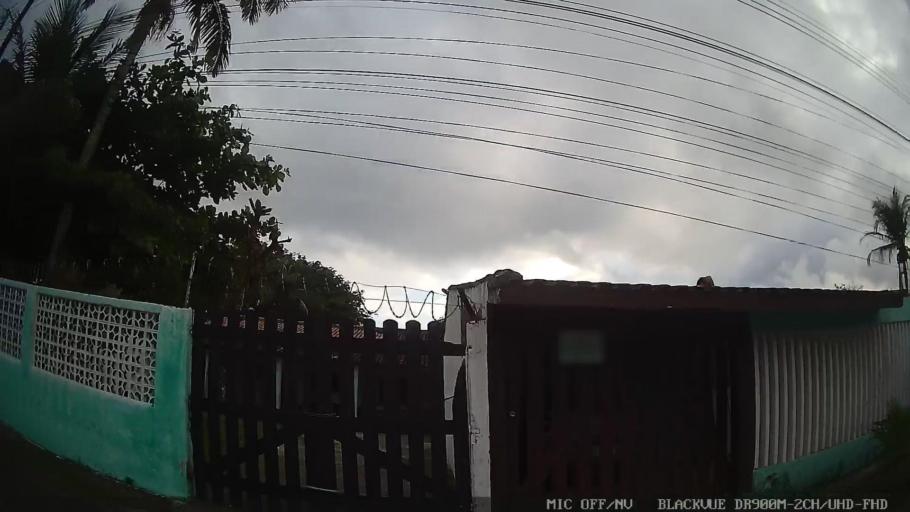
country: BR
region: Sao Paulo
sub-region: Itanhaem
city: Itanhaem
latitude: -24.1922
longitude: -46.8178
